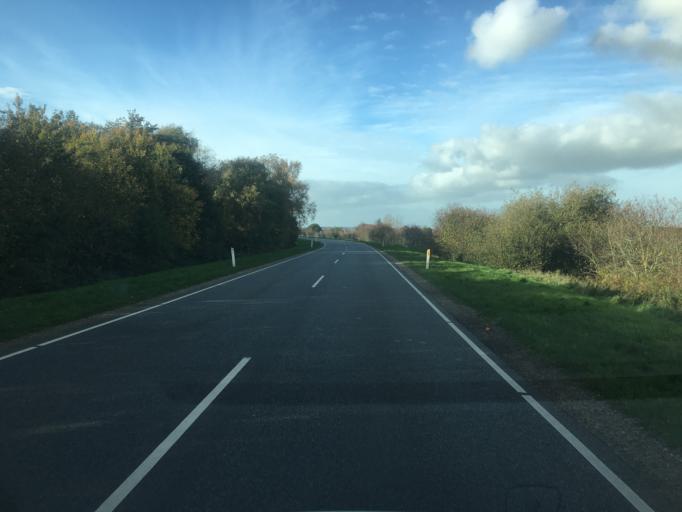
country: DK
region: South Denmark
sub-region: Tonder Kommune
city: Logumkloster
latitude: 55.0605
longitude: 8.9633
